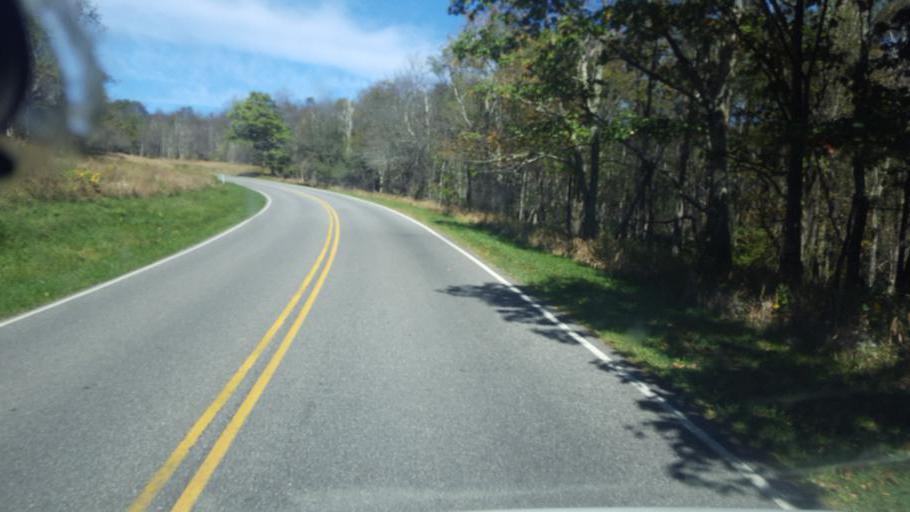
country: US
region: Virginia
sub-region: Page County
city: Stanley
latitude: 38.5083
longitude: -78.4413
